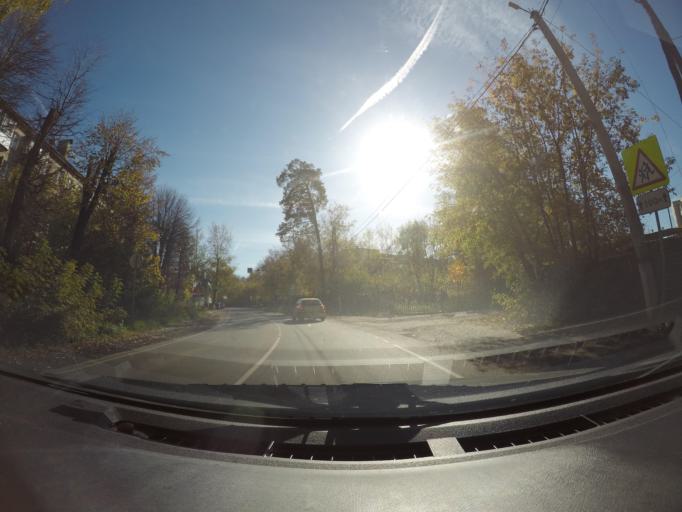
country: RU
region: Moskovskaya
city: Rodniki
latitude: 55.6400
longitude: 38.0532
